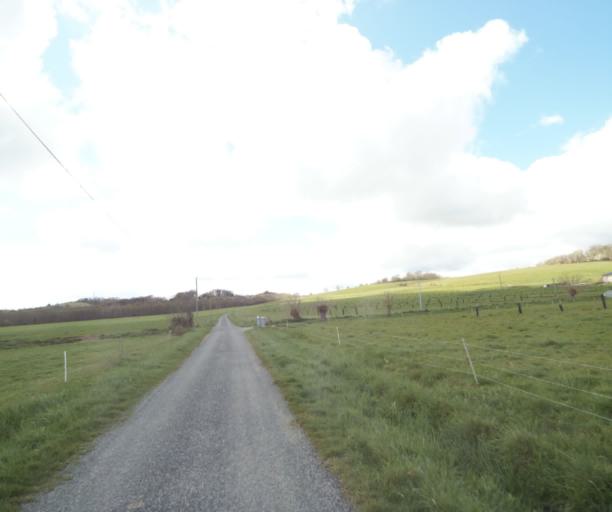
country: FR
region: Midi-Pyrenees
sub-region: Departement de l'Ariege
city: Saverdun
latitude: 43.1940
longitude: 1.5828
